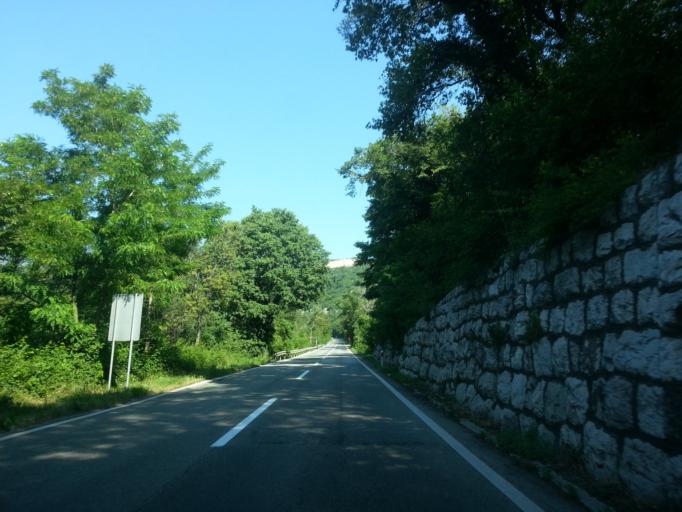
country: HR
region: Primorsko-Goranska
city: Krasica
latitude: 45.3048
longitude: 14.5480
